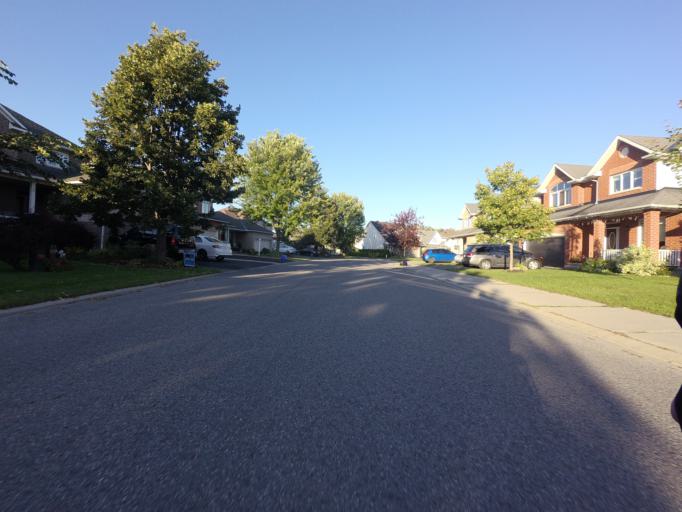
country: CA
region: Ontario
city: Ottawa
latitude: 45.2905
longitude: -75.7088
